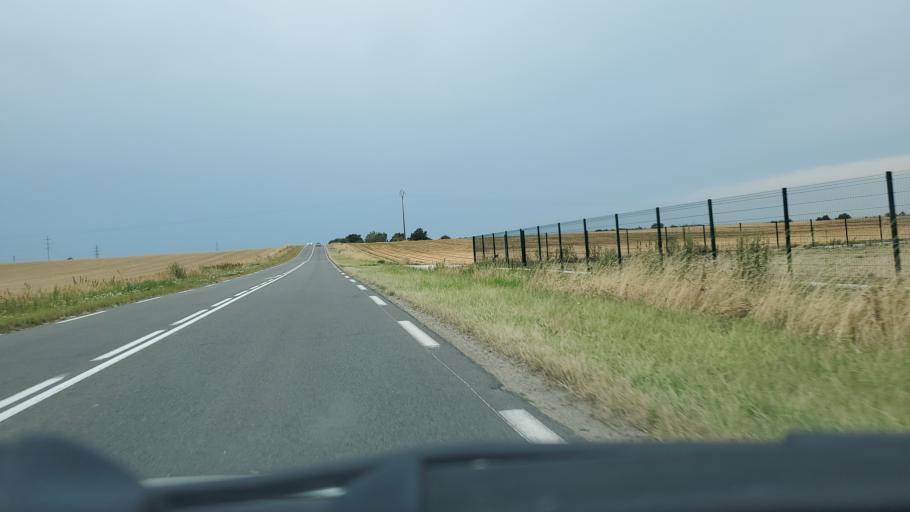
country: FR
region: Ile-de-France
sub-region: Departement de Seine-et-Marne
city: Chailly-en-Brie
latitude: 48.7919
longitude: 3.1145
